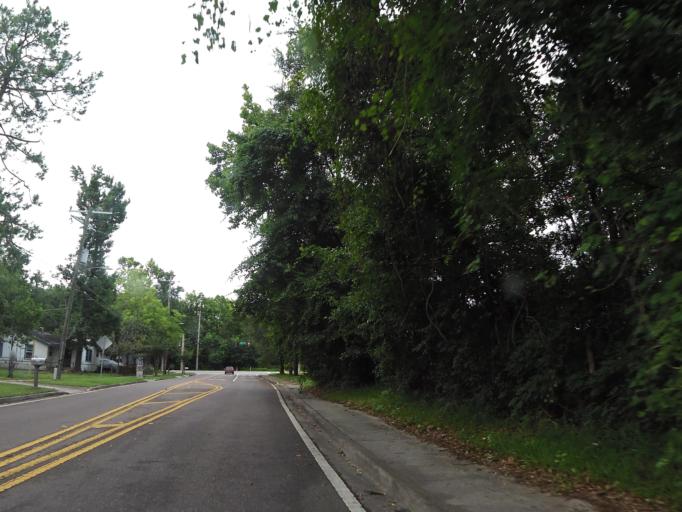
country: US
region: Florida
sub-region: Duval County
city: Jacksonville
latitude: 30.3887
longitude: -81.7247
